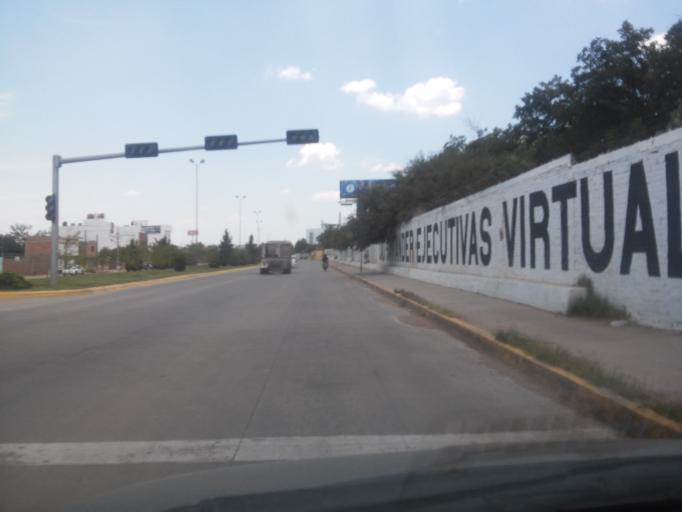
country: MX
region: Durango
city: Victoria de Durango
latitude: 24.0588
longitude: -104.6363
